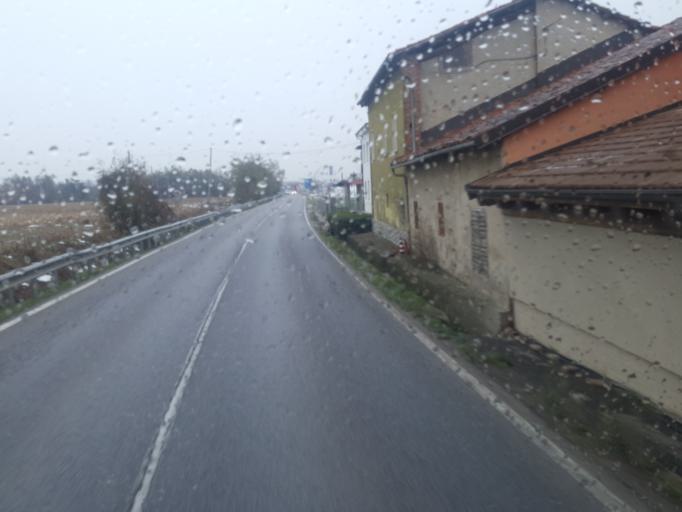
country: IT
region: Piedmont
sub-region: Provincia di Cuneo
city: Breo
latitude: 44.4154
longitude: 7.8437
